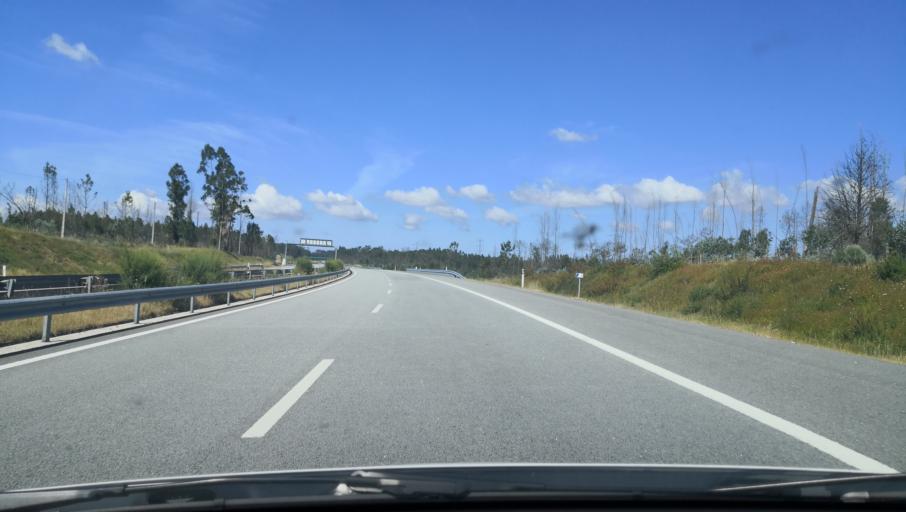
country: PT
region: Coimbra
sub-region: Cantanhede
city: Cantanhede
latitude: 40.2848
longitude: -8.5762
